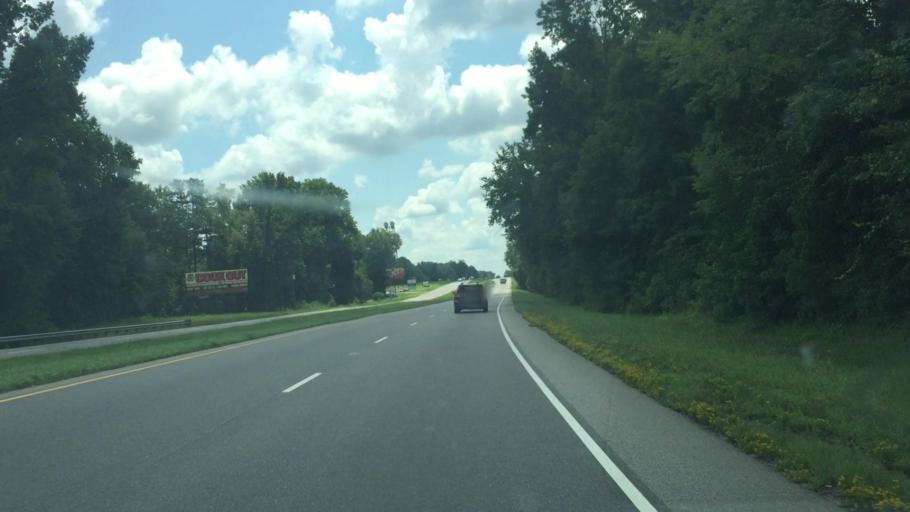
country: US
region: North Carolina
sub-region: Scotland County
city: Laurel Hill
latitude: 34.7978
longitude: -79.5193
